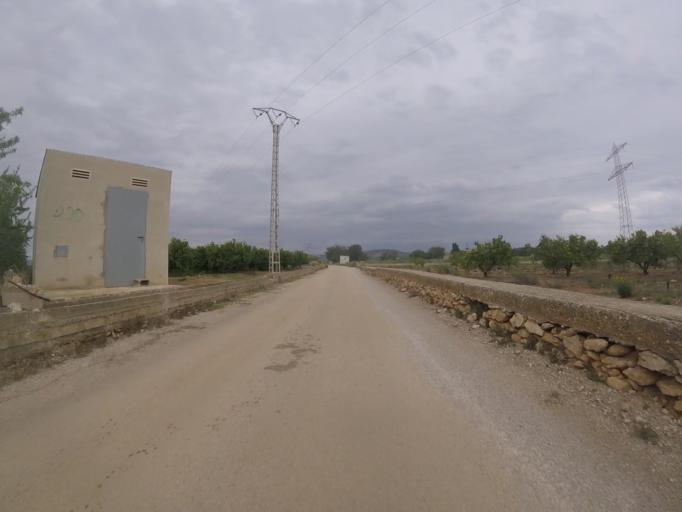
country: ES
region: Valencia
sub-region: Provincia de Castello
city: Torreblanca
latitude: 40.2181
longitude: 0.2239
